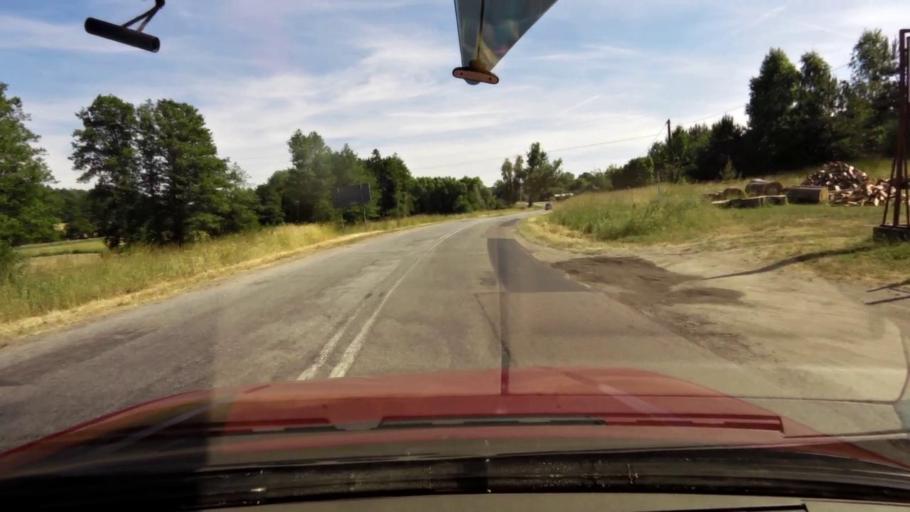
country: PL
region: Pomeranian Voivodeship
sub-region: Powiat slupski
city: Kepice
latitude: 54.2815
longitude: 16.9577
